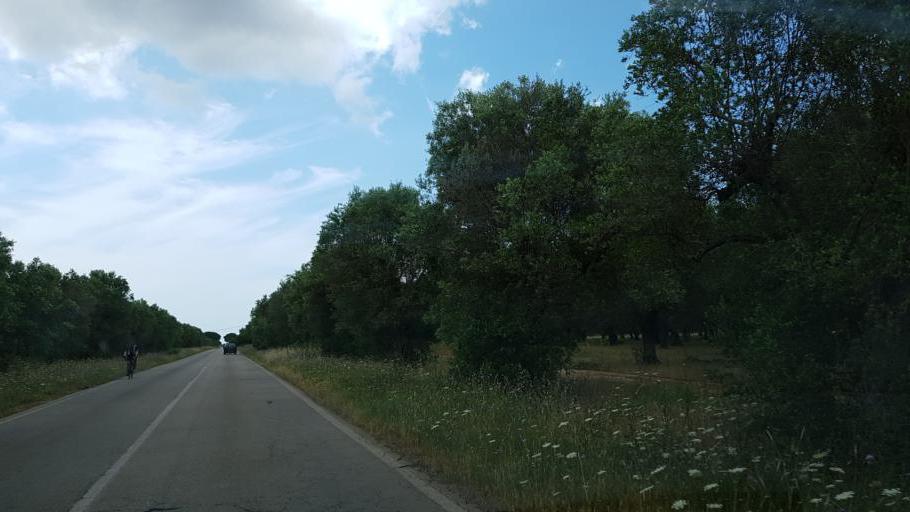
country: IT
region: Apulia
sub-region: Provincia di Brindisi
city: San Pancrazio Salentino
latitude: 40.3504
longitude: 17.8458
